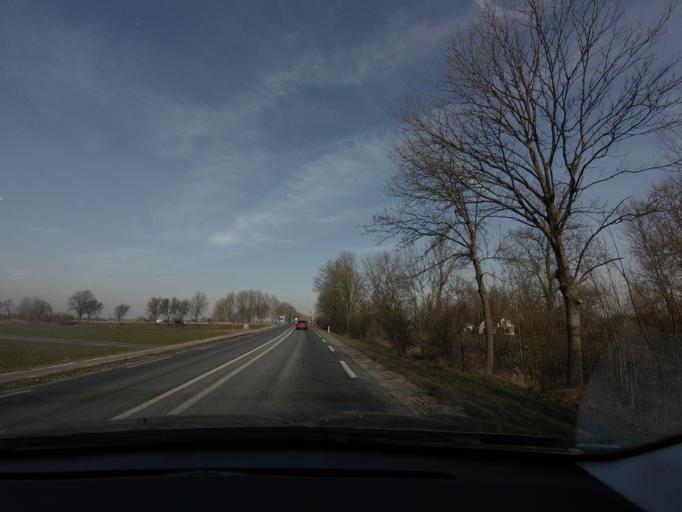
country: NL
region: Utrecht
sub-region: Gemeente De Ronde Venen
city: Mijdrecht
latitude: 52.1603
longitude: 4.9104
